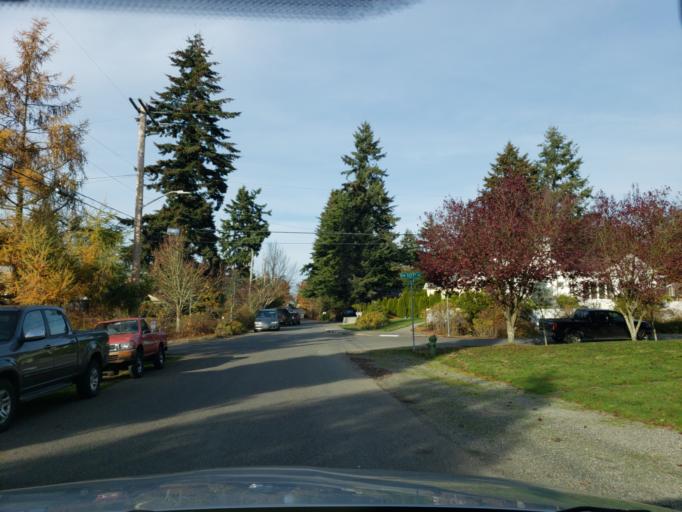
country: US
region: Washington
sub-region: King County
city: Shoreline
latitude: 47.7066
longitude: -122.3581
